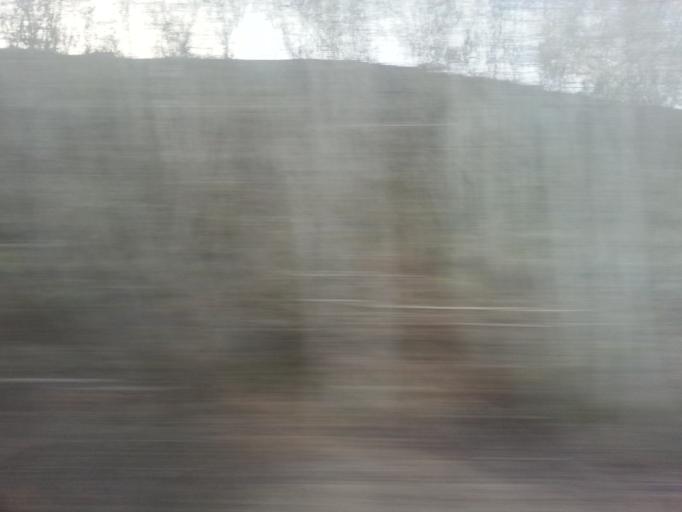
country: NO
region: Sor-Trondelag
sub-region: Melhus
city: Lundamo
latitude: 63.1754
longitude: 10.3065
